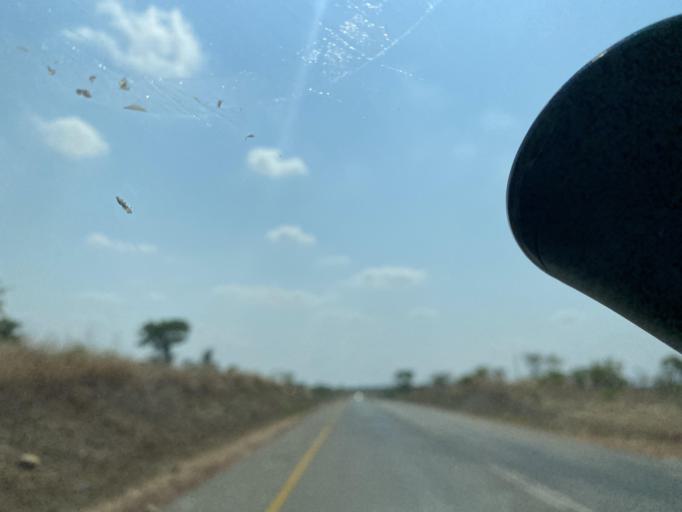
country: ZM
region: Lusaka
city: Chongwe
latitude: -15.5354
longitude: 28.6470
